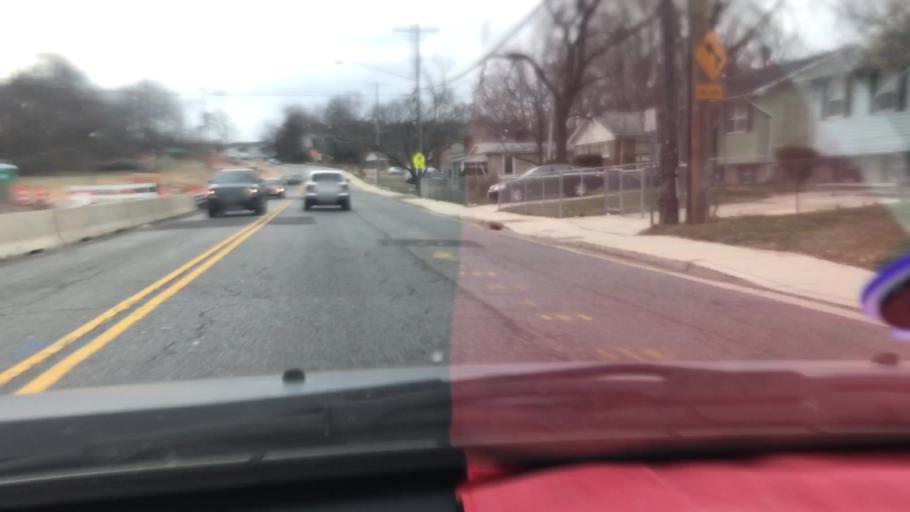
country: US
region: Maryland
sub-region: Prince George's County
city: Peppermill Village
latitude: 38.9067
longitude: -76.8937
